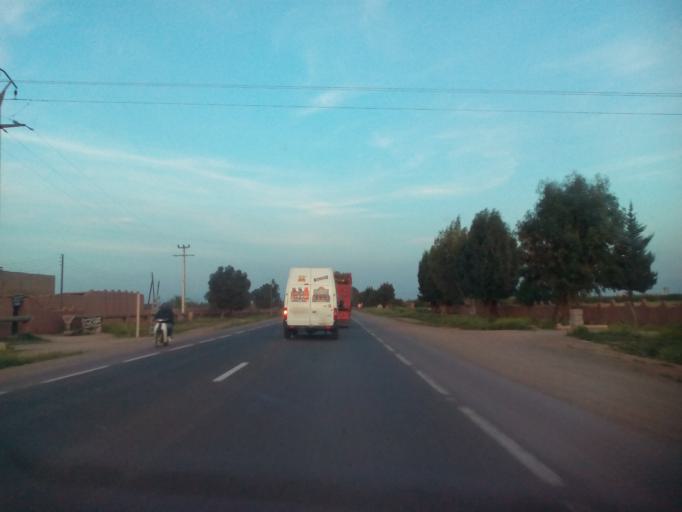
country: MA
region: Marrakech-Tensift-Al Haouz
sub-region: Marrakech
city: Marrakesh
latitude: 31.6340
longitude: -8.2368
